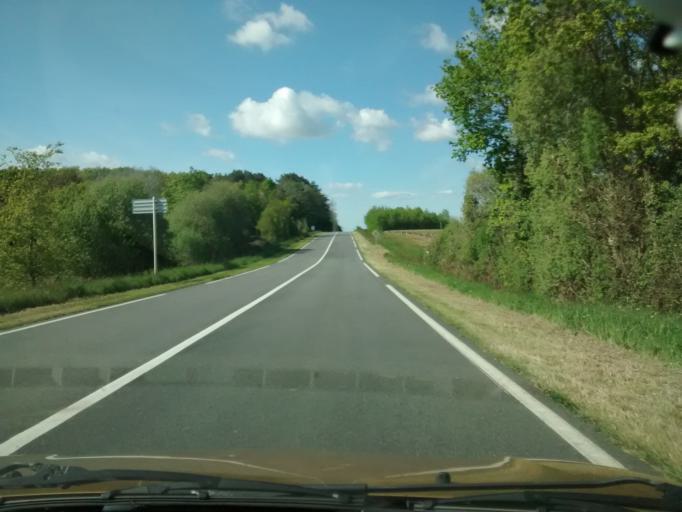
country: FR
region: Pays de la Loire
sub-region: Departement de la Vendee
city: Rocheserviere
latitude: 46.8924
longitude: -1.5018
